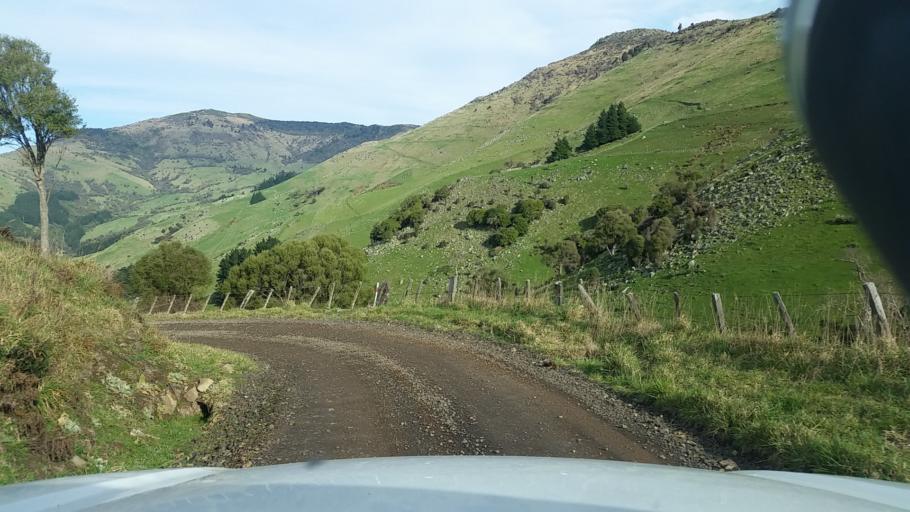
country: NZ
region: Canterbury
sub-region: Christchurch City
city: Christchurch
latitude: -43.6809
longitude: 172.8533
